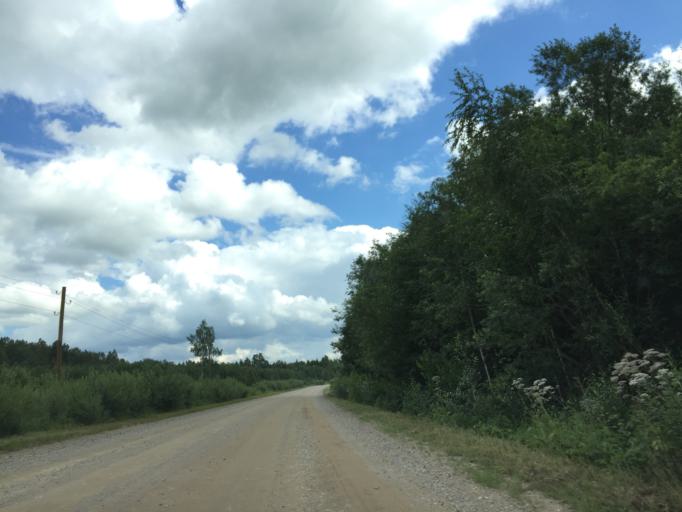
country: LV
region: Malpils
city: Malpils
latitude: 56.8781
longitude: 24.9962
